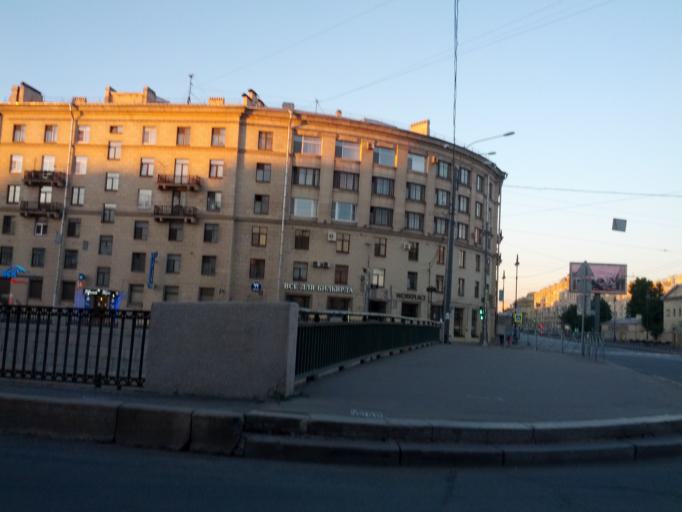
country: RU
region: St.-Petersburg
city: Saint Petersburg
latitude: 59.9089
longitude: 30.3188
